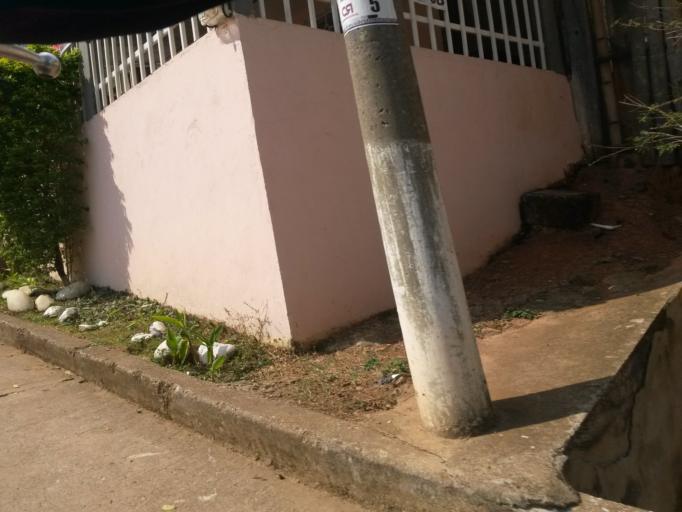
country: CO
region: Cauca
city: Buenos Aires
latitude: 3.0167
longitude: -76.6434
